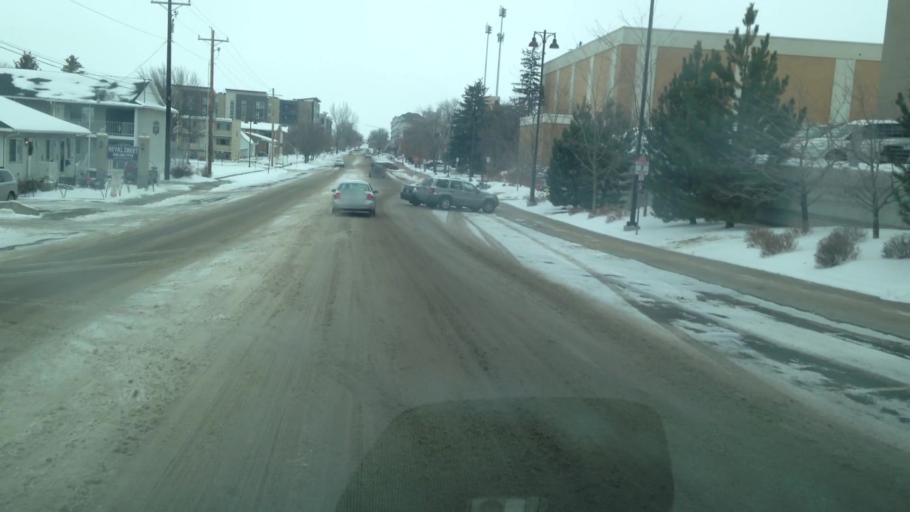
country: US
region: Idaho
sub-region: Madison County
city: Rexburg
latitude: 43.8184
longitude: -111.7867
